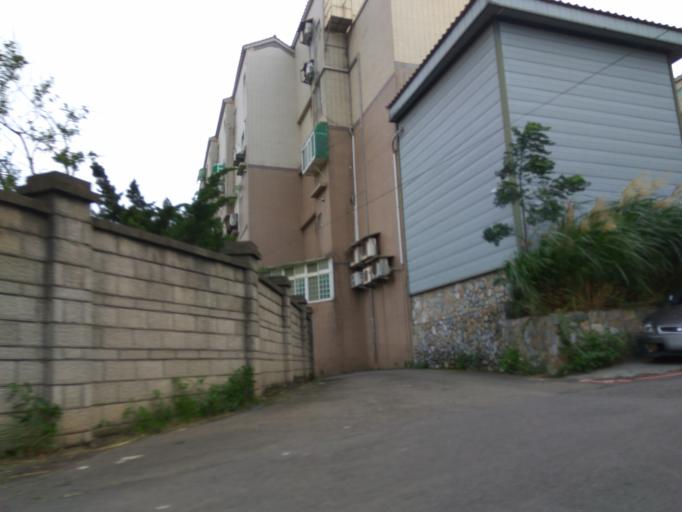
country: TW
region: Taiwan
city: Daxi
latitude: 24.9416
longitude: 121.2038
